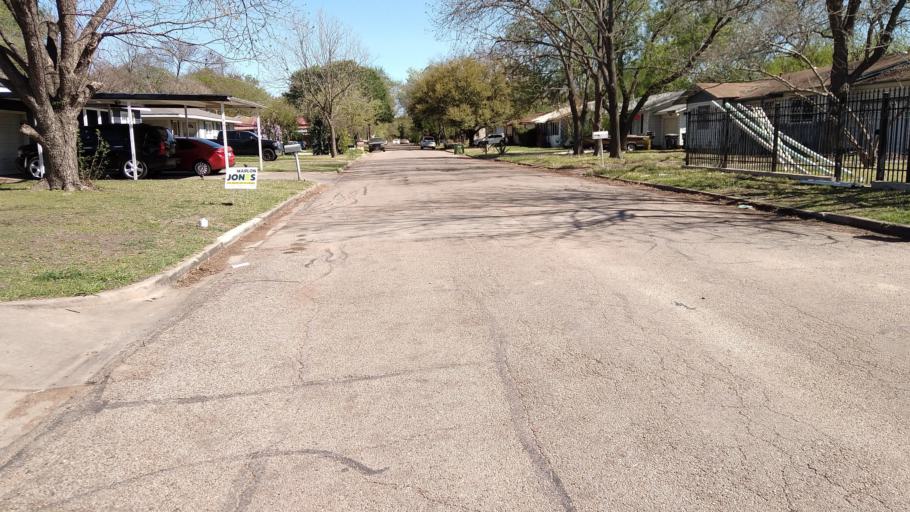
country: US
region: Texas
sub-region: McLennan County
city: Beverly
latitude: 31.5216
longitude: -97.1293
